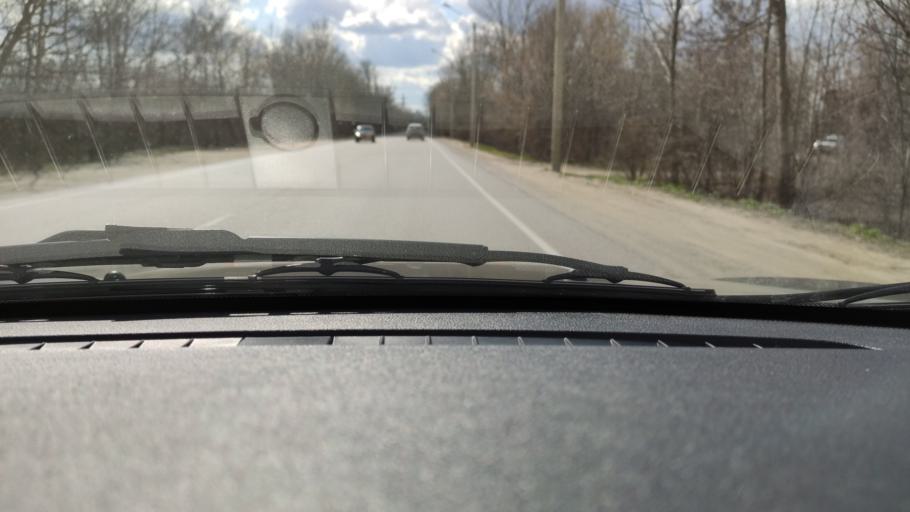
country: RU
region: Voronezj
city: Voronezh
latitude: 51.5988
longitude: 39.1770
